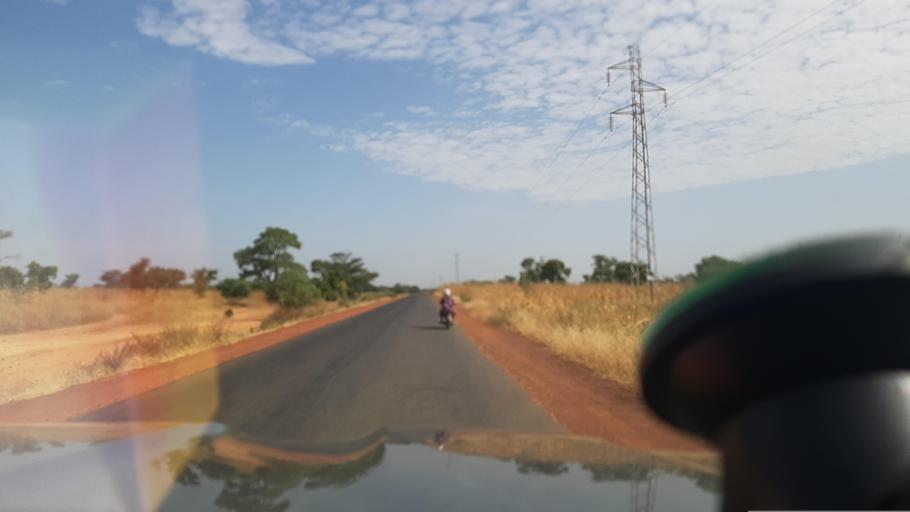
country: ML
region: Segou
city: Markala
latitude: 13.5590
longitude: -6.1127
